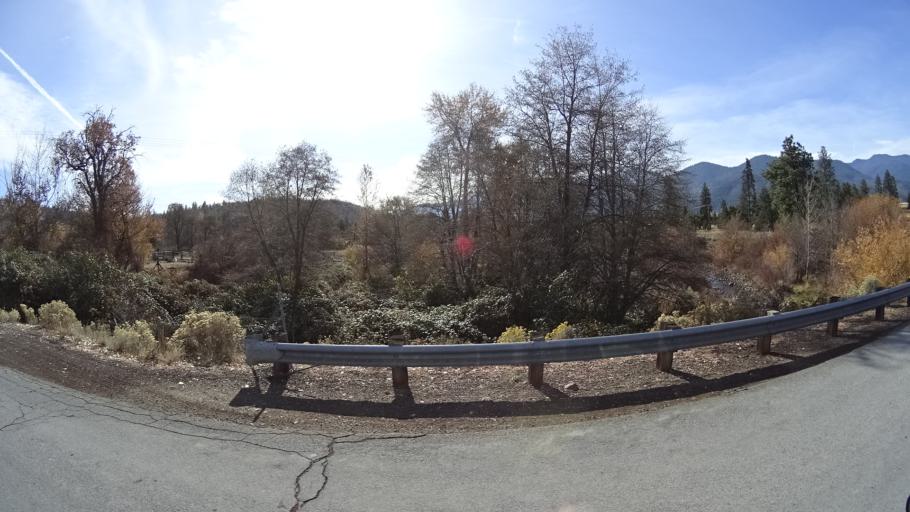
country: US
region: California
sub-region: Siskiyou County
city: Weed
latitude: 41.4474
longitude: -122.4313
